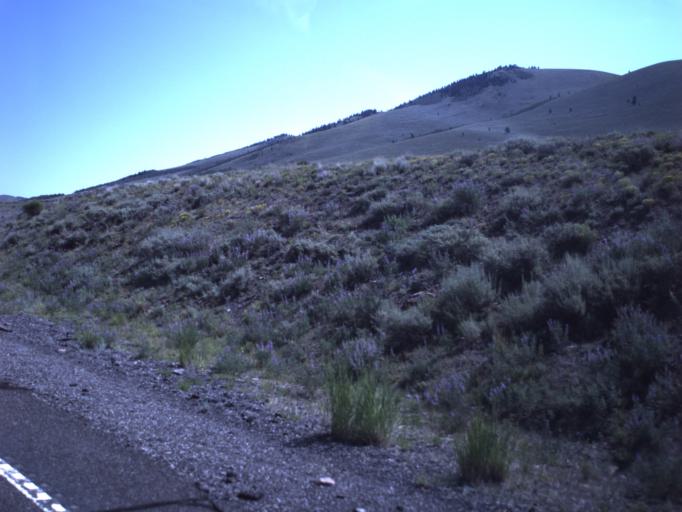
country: US
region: Utah
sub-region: Wayne County
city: Loa
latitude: 38.5497
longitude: -111.5103
